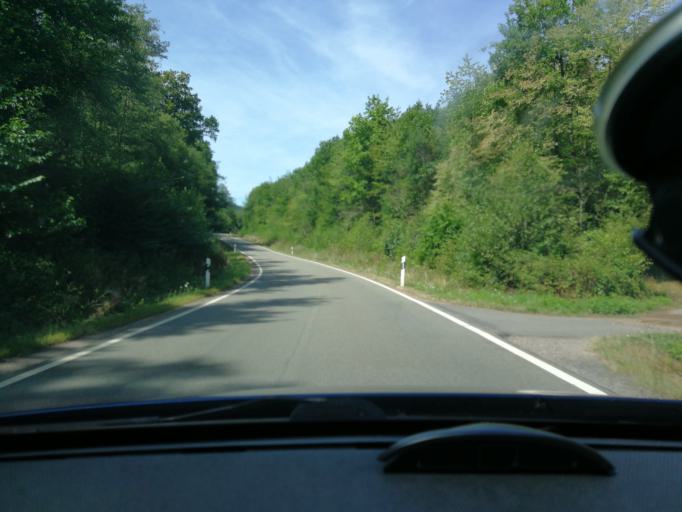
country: DE
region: Rheinland-Pfalz
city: Sehlem
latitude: 49.9084
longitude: 6.8182
